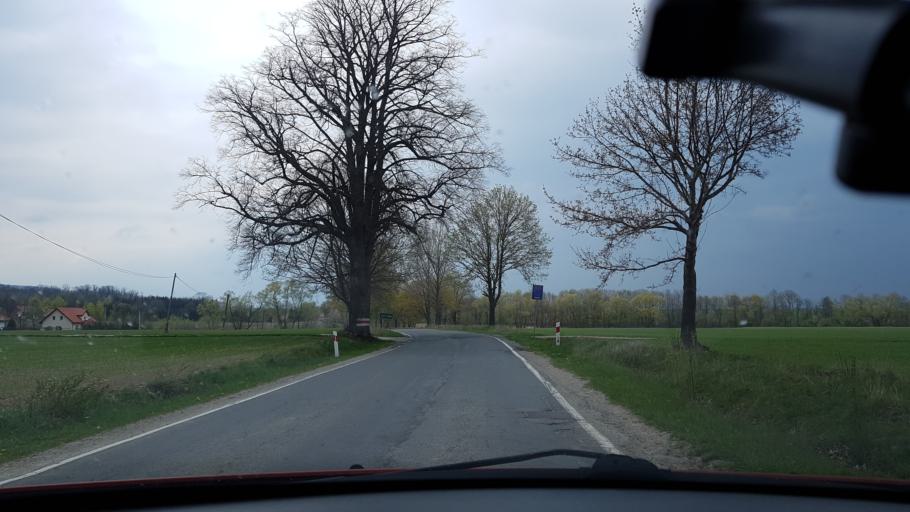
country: PL
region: Lower Silesian Voivodeship
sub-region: Powiat klodzki
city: Bystrzyca Klodzka
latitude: 50.3316
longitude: 16.6016
